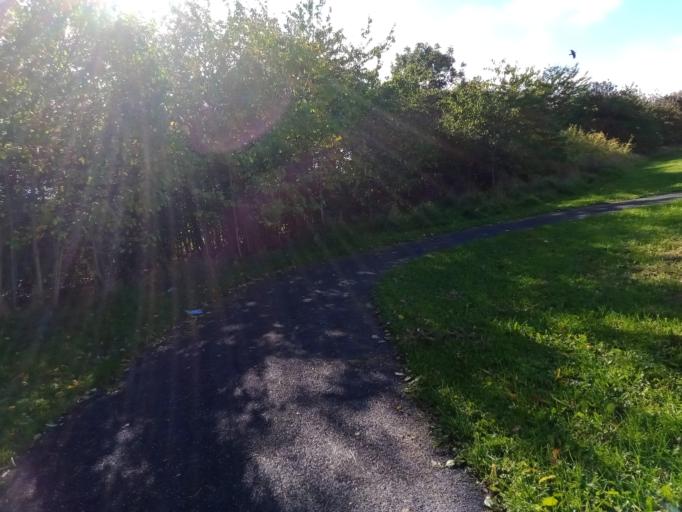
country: IE
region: Leinster
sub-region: Kilkenny
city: Kilkenny
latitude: 52.6330
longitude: -7.2361
